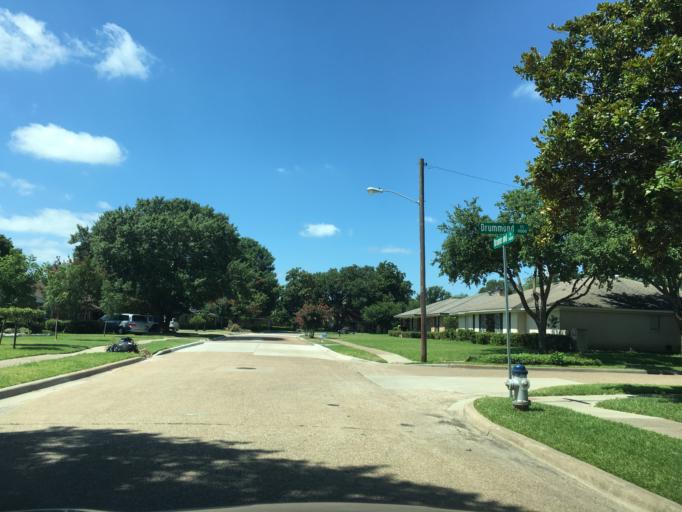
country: US
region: Texas
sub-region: Dallas County
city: Garland
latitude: 32.8487
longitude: -96.6508
